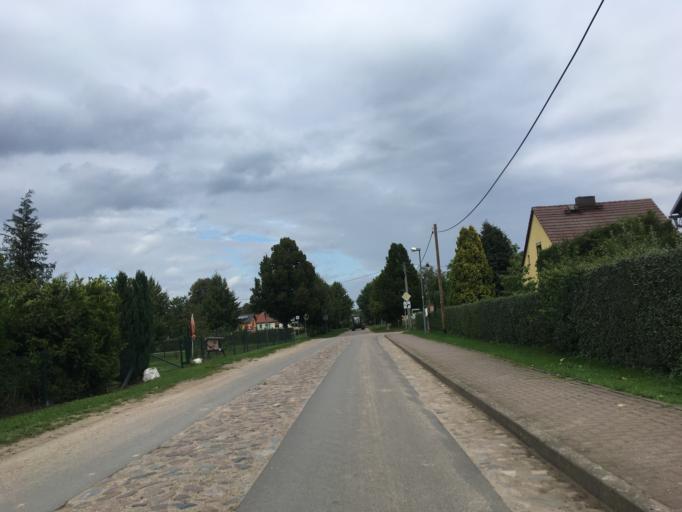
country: DE
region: Brandenburg
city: Joachimsthal
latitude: 53.0248
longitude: 13.7632
